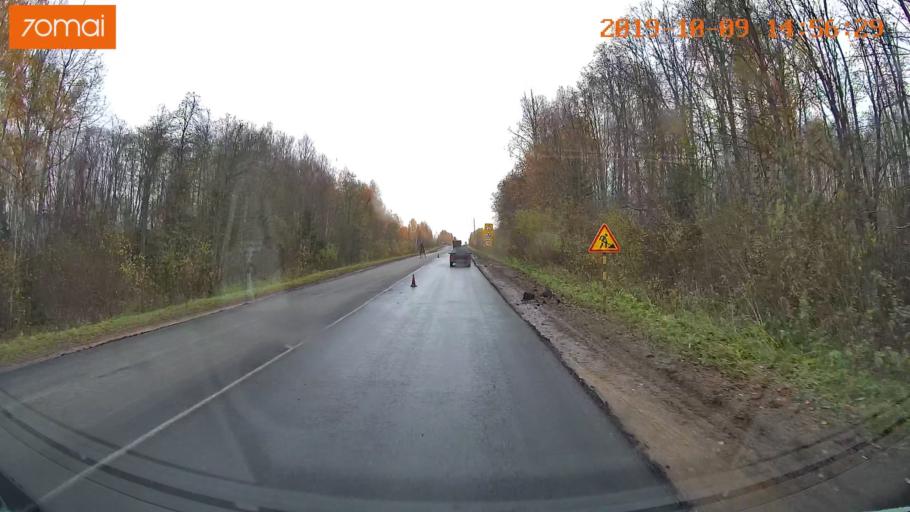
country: RU
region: Kostroma
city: Chistyye Bory
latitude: 58.3455
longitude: 41.6474
